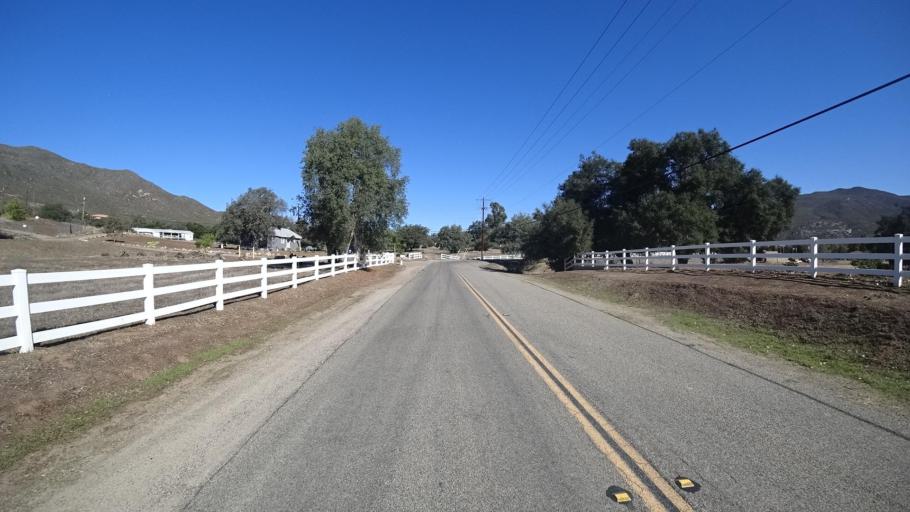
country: US
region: California
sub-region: San Diego County
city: Alpine
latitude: 32.8530
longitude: -116.7025
